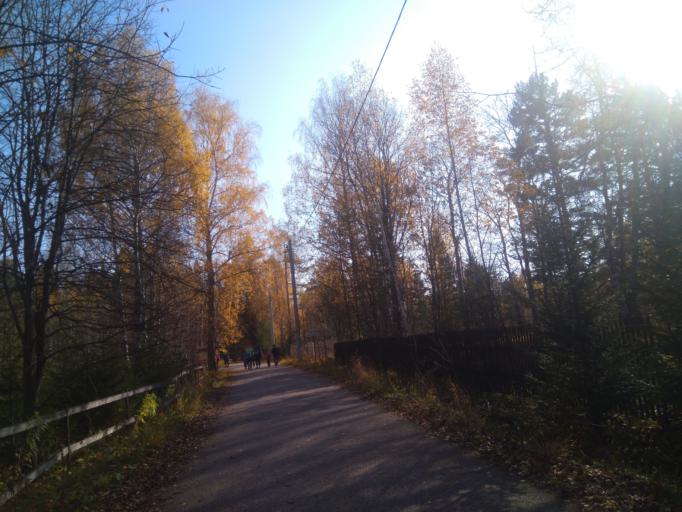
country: RU
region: Sverdlovsk
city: Mikhaylovsk
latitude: 56.5232
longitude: 59.2329
